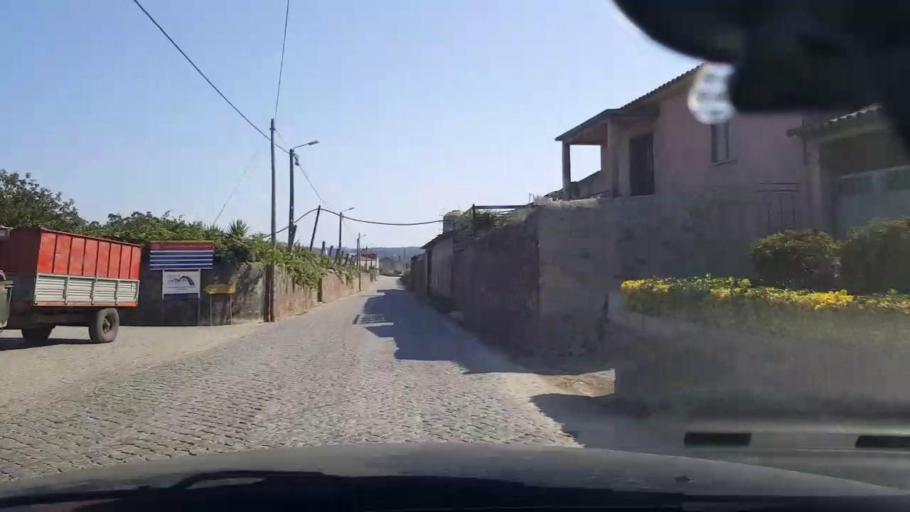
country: PT
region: Porto
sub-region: Povoa de Varzim
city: Pedroso
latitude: 41.4069
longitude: -8.6923
